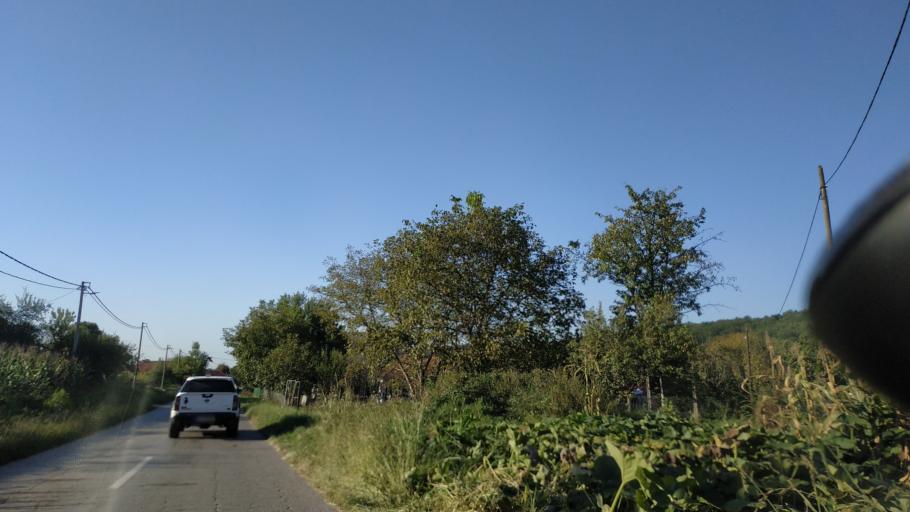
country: RS
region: Central Serbia
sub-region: Rasinski Okrug
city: Krusevac
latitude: 43.4876
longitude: 21.3472
